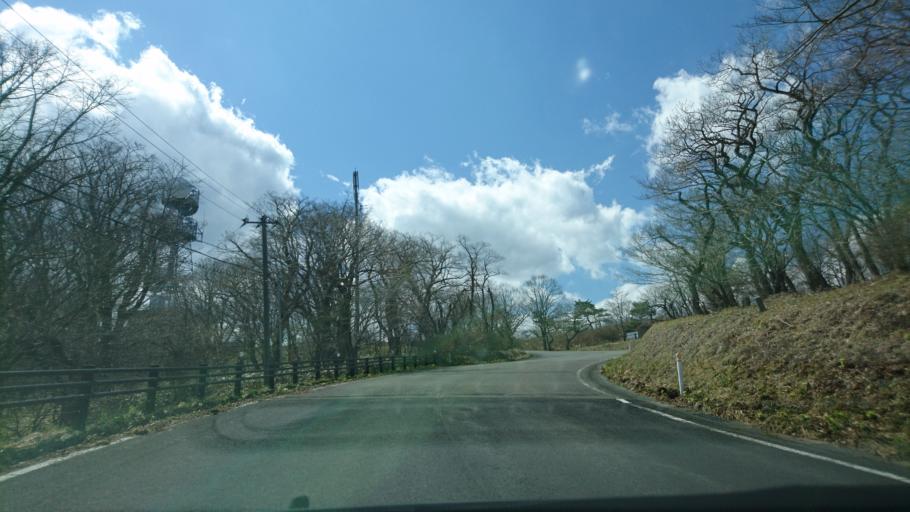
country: JP
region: Iwate
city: Ofunato
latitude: 38.9731
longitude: 141.4468
